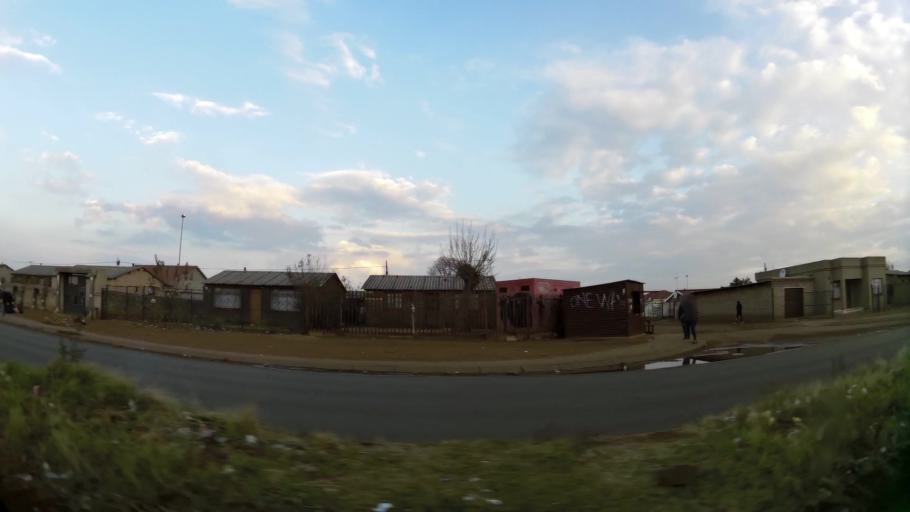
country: ZA
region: Gauteng
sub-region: City of Johannesburg Metropolitan Municipality
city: Orange Farm
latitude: -26.5698
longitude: 27.8451
